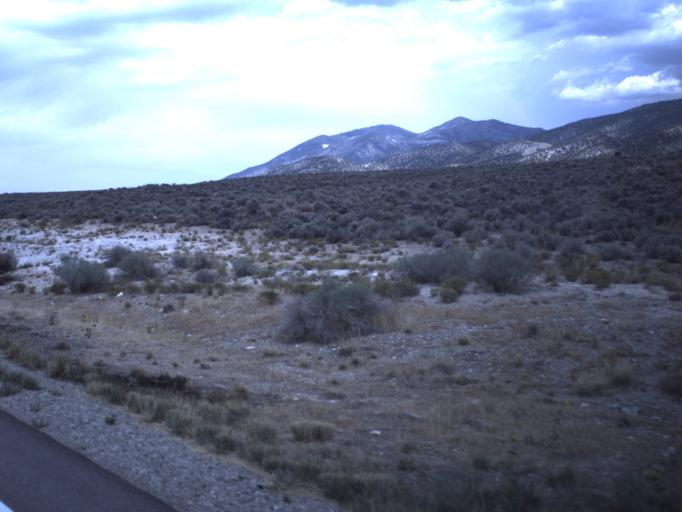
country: US
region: Utah
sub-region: Tooele County
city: Tooele
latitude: 40.2894
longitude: -112.2692
